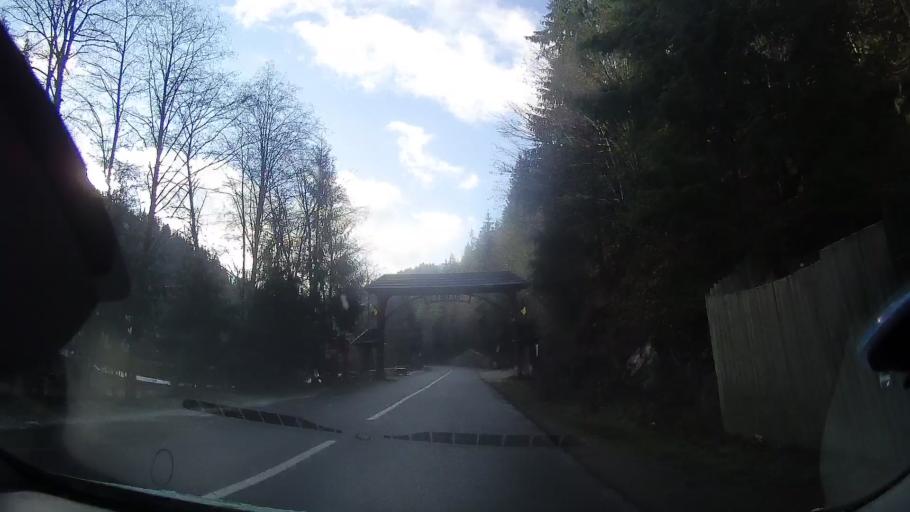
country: RO
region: Alba
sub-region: Comuna Albac
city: Albac
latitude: 46.4313
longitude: 22.9650
